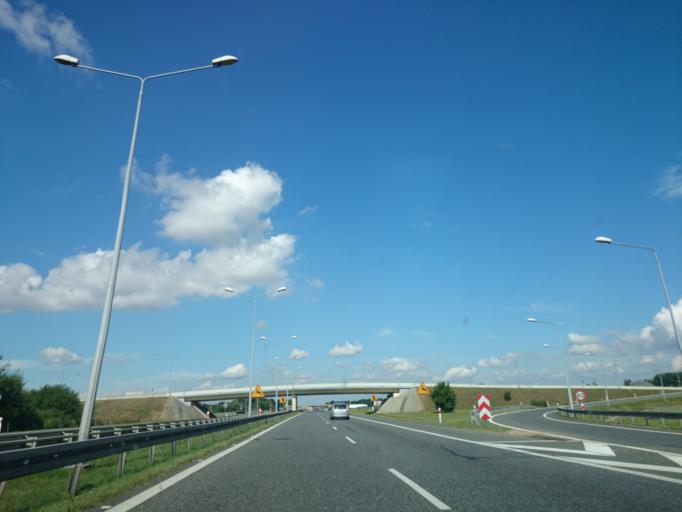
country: PL
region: Opole Voivodeship
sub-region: Powiat brzeski
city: Grodkow
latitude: 50.7801
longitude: 17.3524
